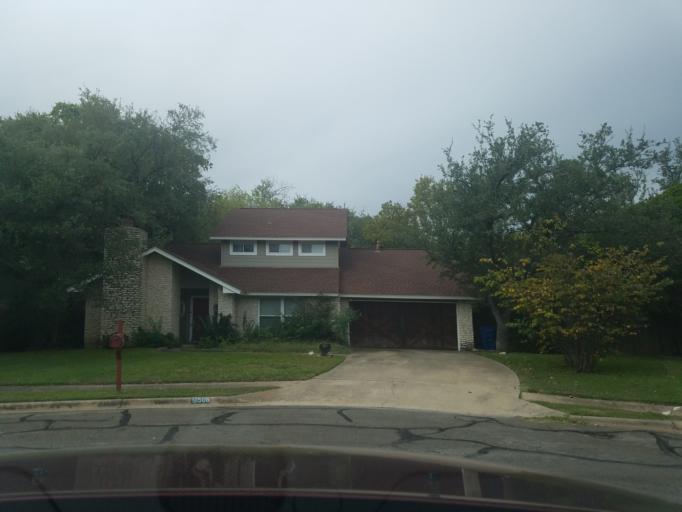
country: US
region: Texas
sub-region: Williamson County
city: Anderson Mill
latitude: 30.4645
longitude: -97.8066
